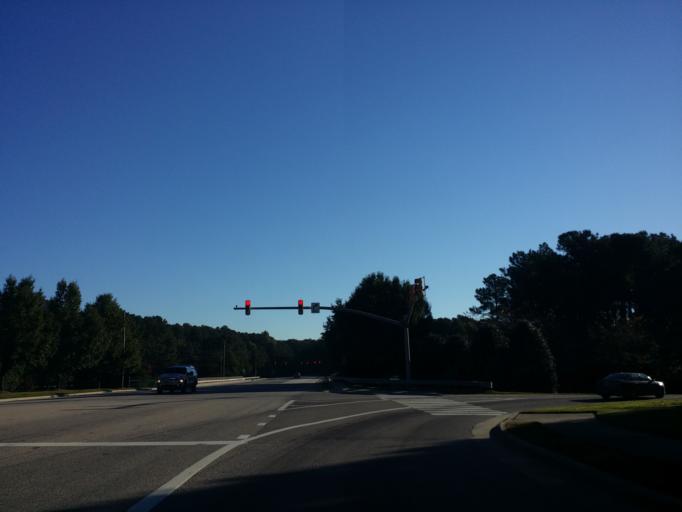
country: US
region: North Carolina
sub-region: Wake County
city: Cary
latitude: 35.8311
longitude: -78.7651
